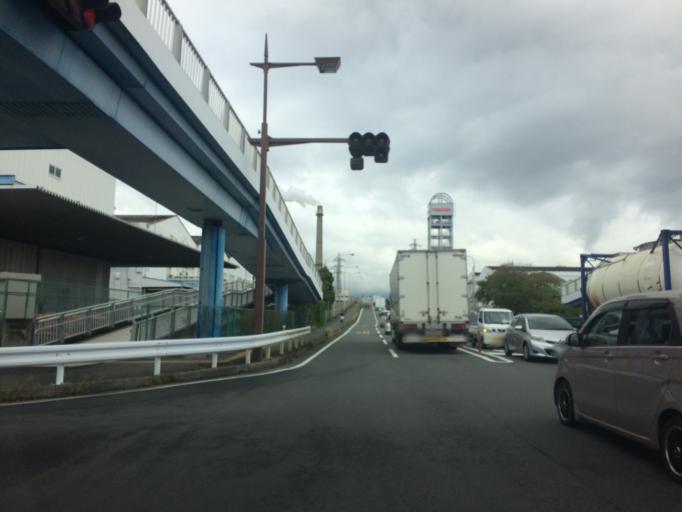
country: JP
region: Shizuoka
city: Fuji
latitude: 35.1479
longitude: 138.6633
